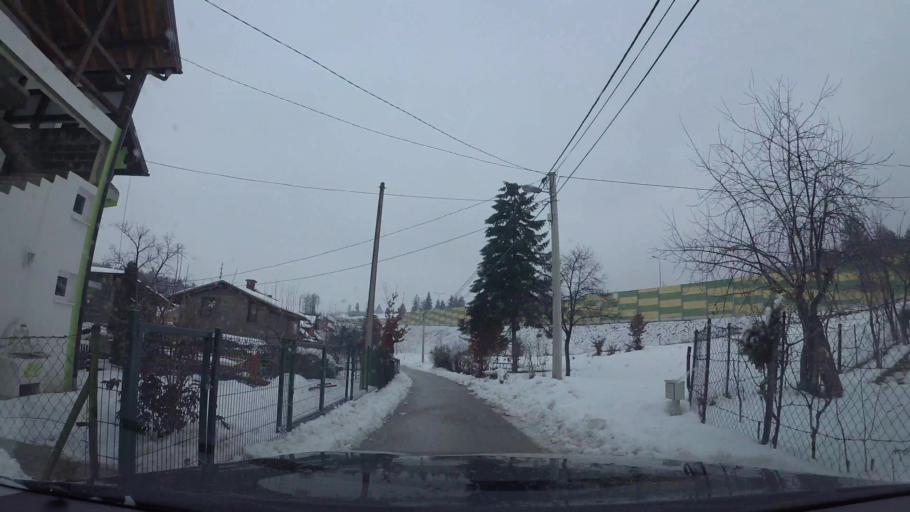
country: BA
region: Federation of Bosnia and Herzegovina
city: Hadzici
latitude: 43.8619
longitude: 18.2696
